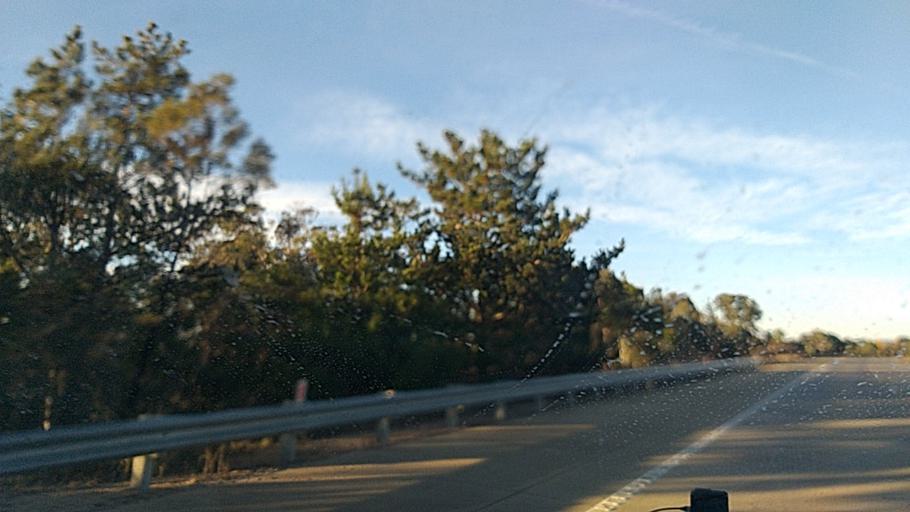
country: AU
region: New South Wales
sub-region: Yass Valley
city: Gundaroo
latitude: -35.1349
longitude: 149.3399
